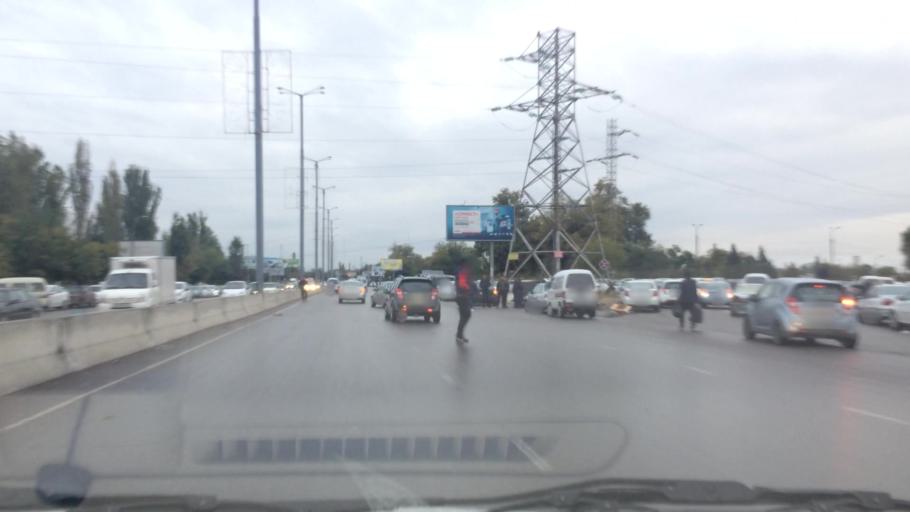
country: UZ
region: Toshkent Shahri
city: Tashkent
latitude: 41.2417
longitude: 69.1708
